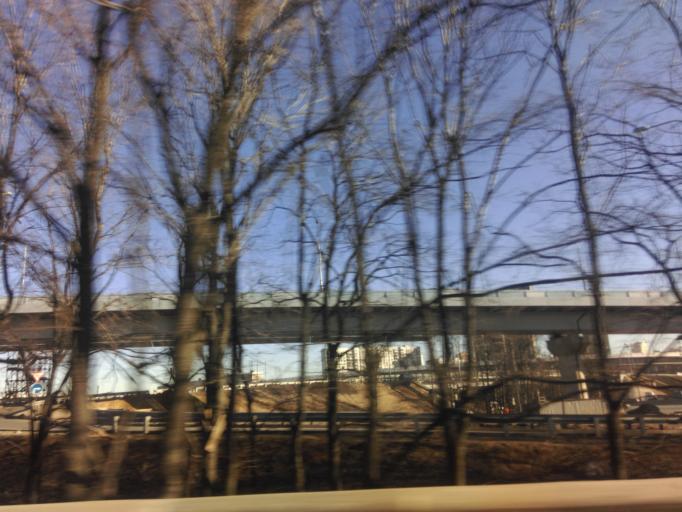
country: RU
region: Moskovskaya
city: Marfino
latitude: 55.7123
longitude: 37.3844
